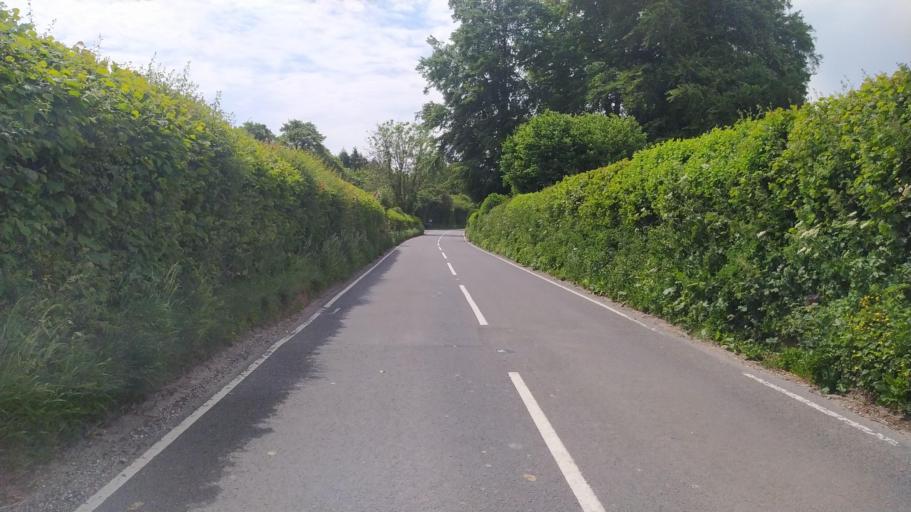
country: GB
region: England
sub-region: Dorset
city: Dorchester
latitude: 50.7892
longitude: -2.4735
